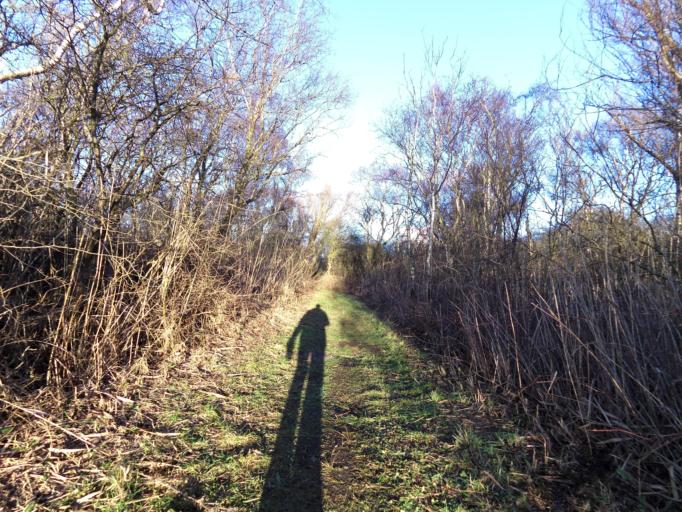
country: NL
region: South Holland
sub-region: Gemeente Hellevoetsluis
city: Nieuw-Helvoet
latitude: 51.8987
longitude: 4.0455
